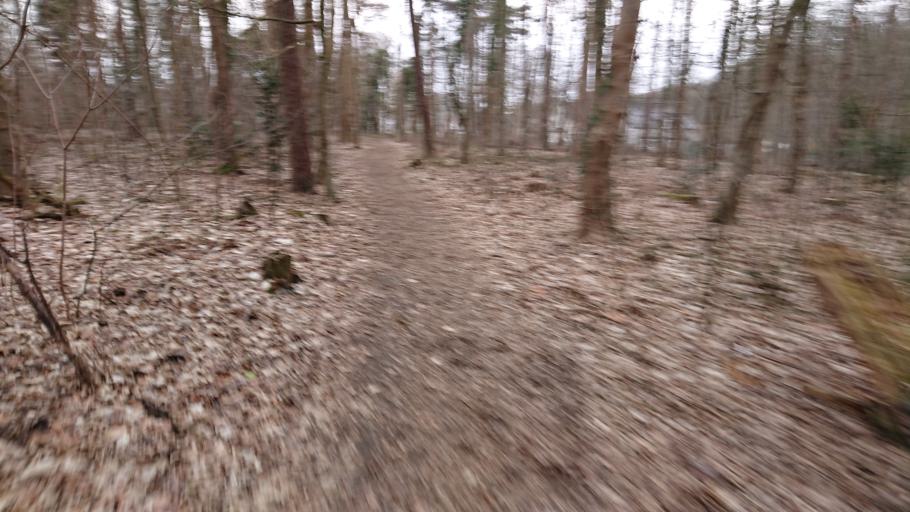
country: DE
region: North Rhine-Westphalia
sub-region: Regierungsbezirk Koln
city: Muelheim
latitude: 51.0051
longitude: 7.0441
